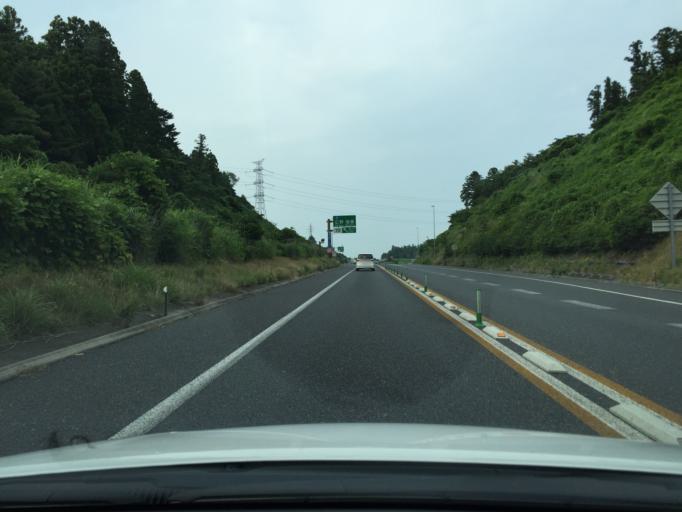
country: JP
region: Fukushima
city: Iwaki
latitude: 37.2339
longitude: 140.9813
